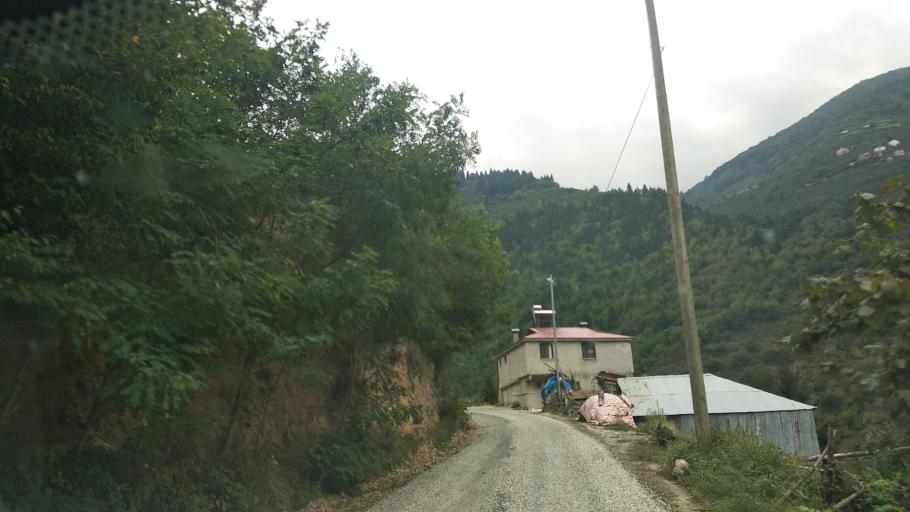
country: TR
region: Giresun
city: Dogankent
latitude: 40.7407
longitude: 38.9863
